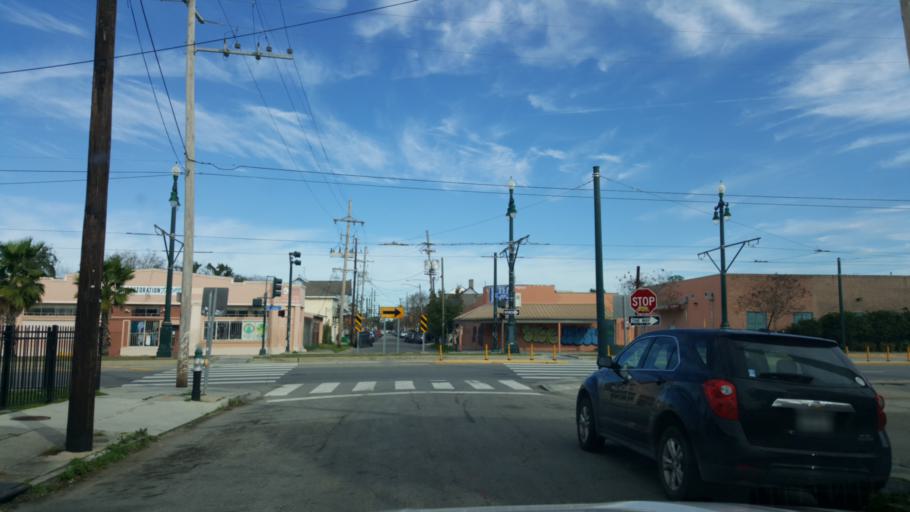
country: US
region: Louisiana
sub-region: Orleans Parish
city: New Orleans
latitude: 29.9681
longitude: -90.0581
